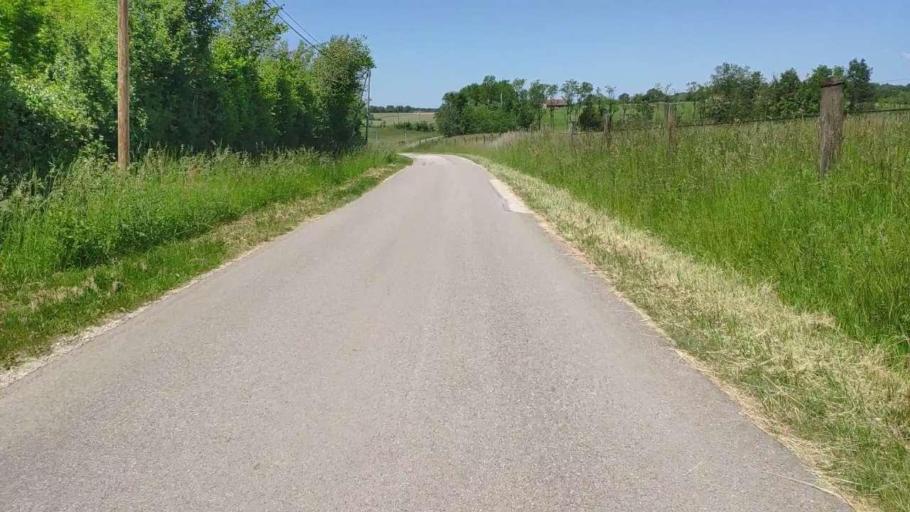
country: FR
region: Franche-Comte
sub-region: Departement du Jura
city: Bletterans
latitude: 46.7475
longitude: 5.4279
